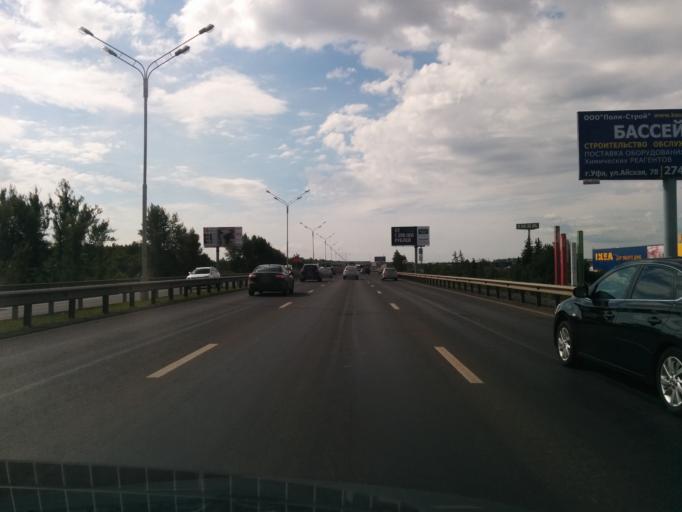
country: RU
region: Bashkortostan
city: Ufa
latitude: 54.6760
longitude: 55.9334
